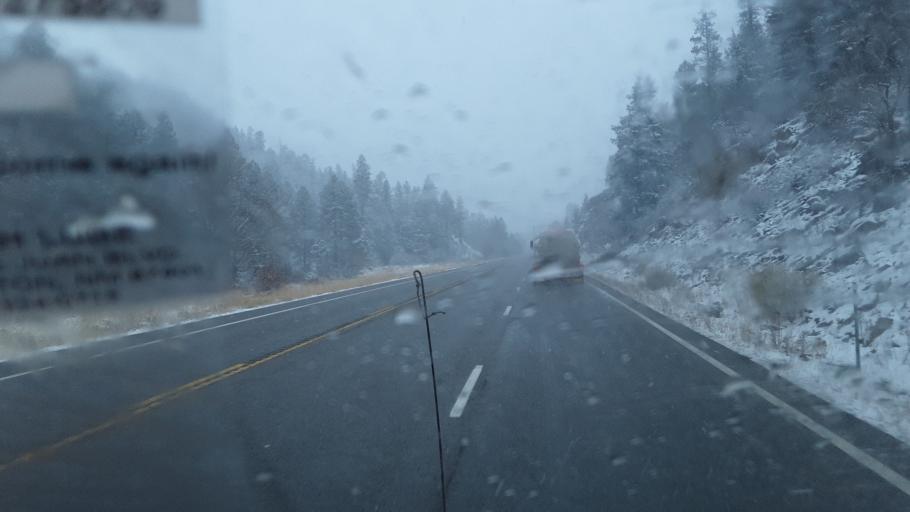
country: US
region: Colorado
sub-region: La Plata County
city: Bayfield
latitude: 37.2317
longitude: -107.4179
